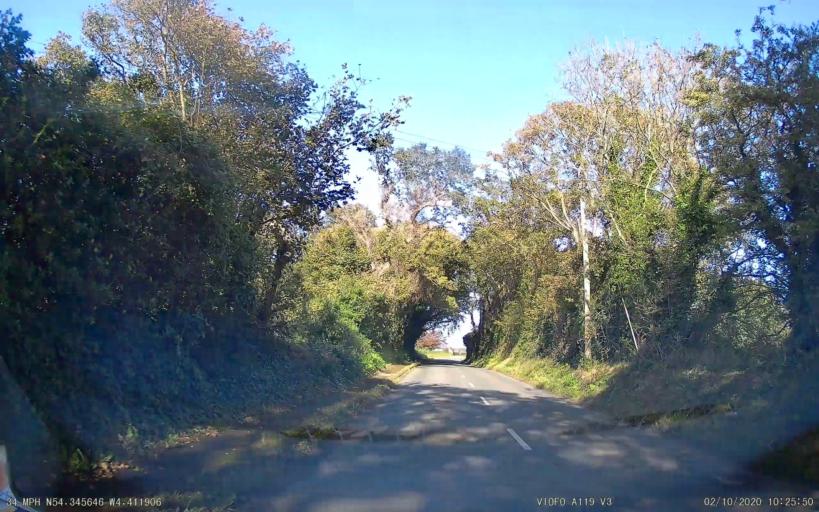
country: IM
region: Ramsey
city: Ramsey
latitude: 54.3456
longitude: -4.4119
